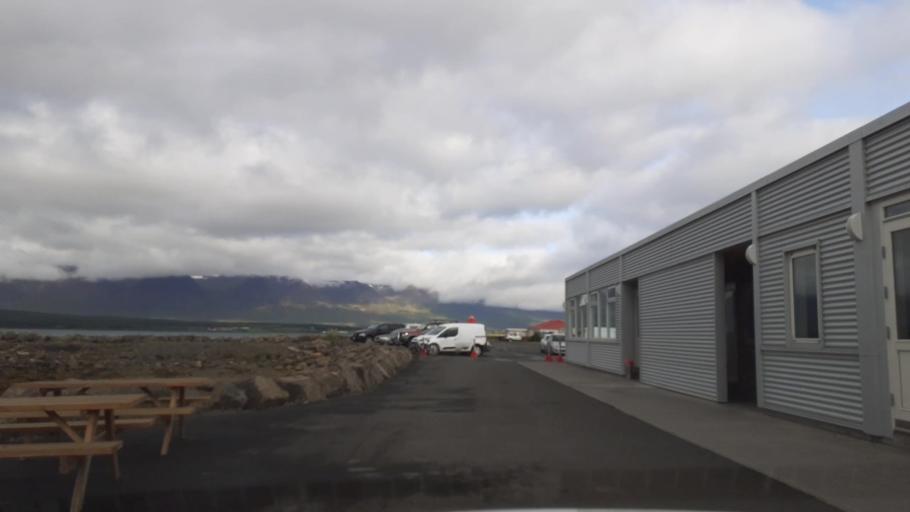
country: IS
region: Northeast
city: Akureyri
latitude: 65.7427
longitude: -18.0872
